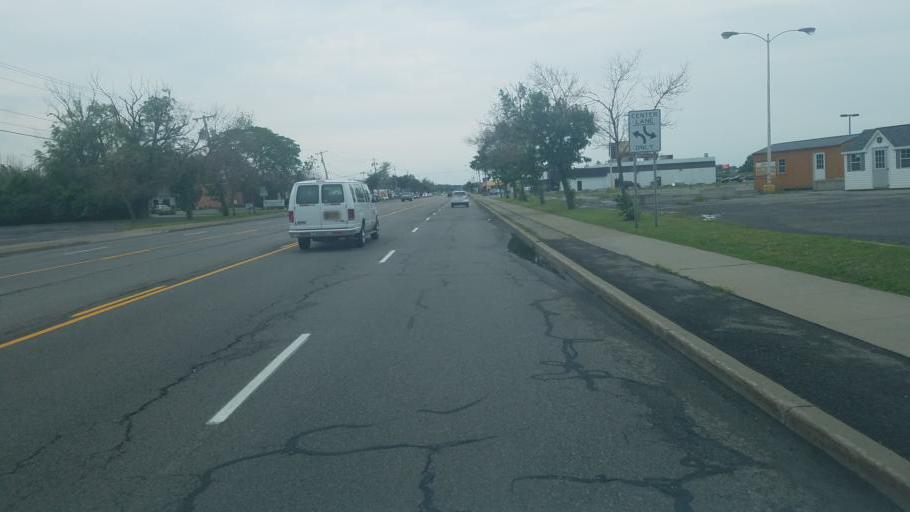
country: US
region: New York
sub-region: Niagara County
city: Niagara Falls
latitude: 43.1068
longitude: -78.9844
